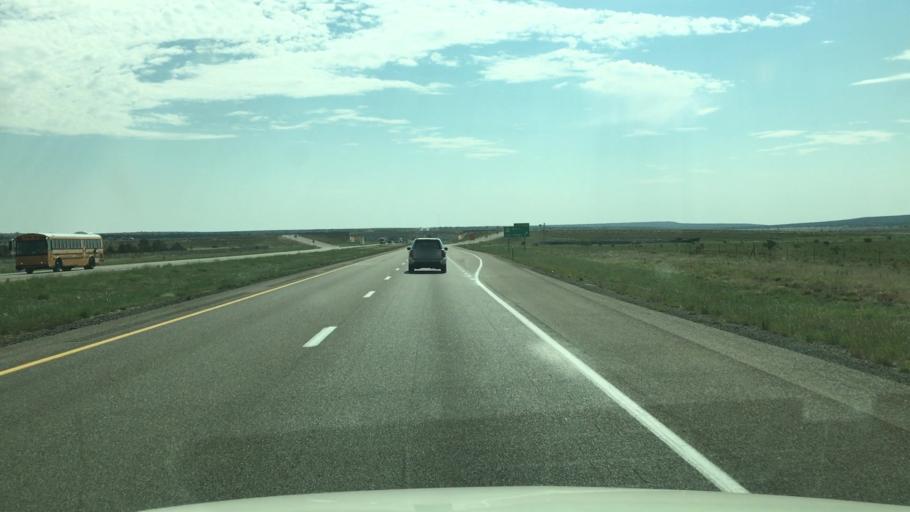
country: US
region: New Mexico
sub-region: Guadalupe County
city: Santa Rosa
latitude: 34.9767
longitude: -104.9977
